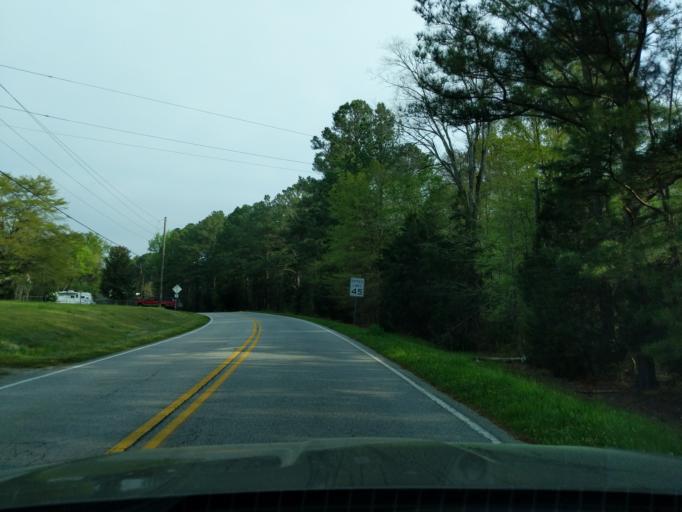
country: US
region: Georgia
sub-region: Columbia County
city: Appling
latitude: 33.5574
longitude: -82.3185
